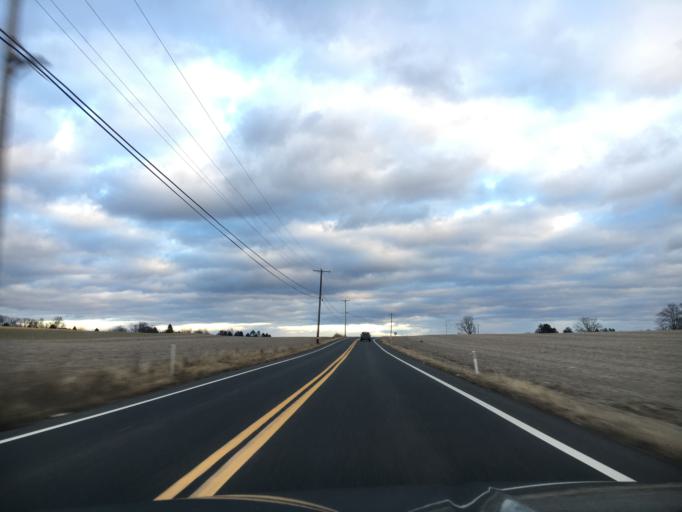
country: US
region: Pennsylvania
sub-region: Lehigh County
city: Schnecksville
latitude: 40.6852
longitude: -75.6690
